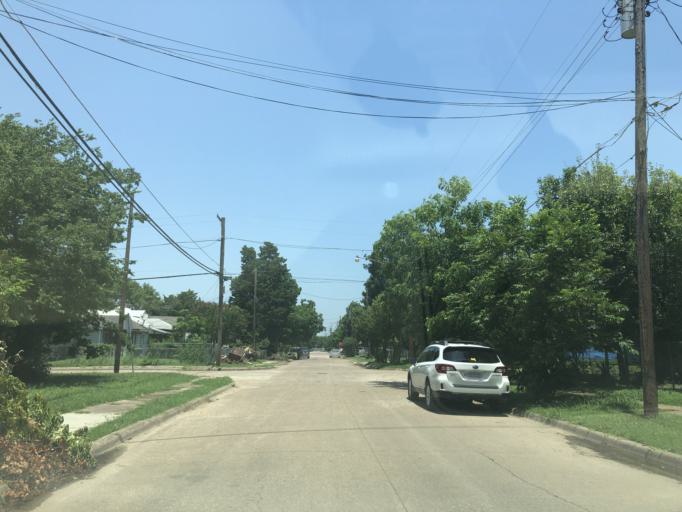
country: US
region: Texas
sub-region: Dallas County
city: Dallas
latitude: 32.7801
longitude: -96.8409
